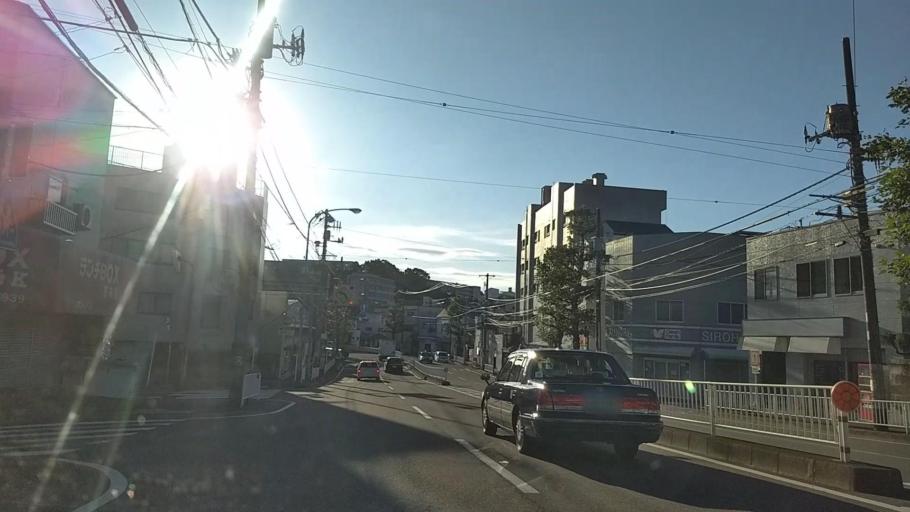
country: JP
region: Kanagawa
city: Yokohama
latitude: 35.4519
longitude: 139.6220
